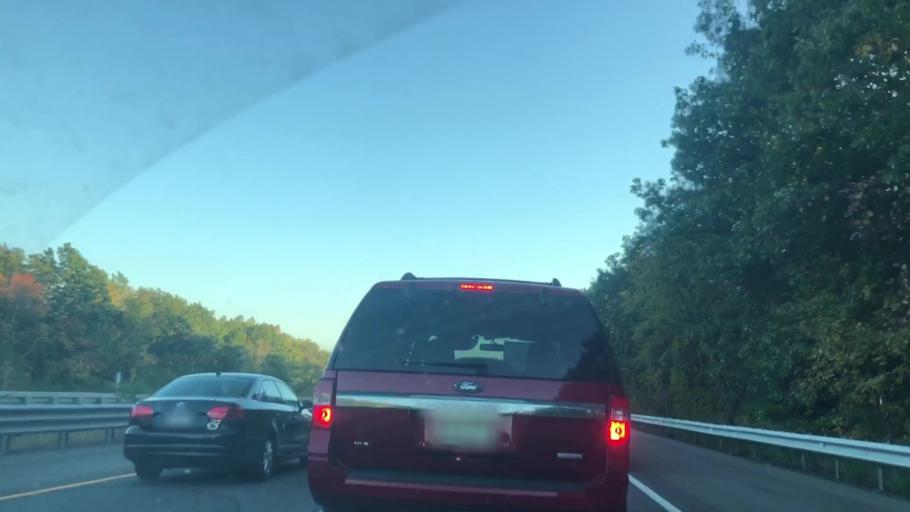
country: US
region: Massachusetts
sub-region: Franklin County
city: South Deerfield
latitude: 42.5259
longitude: -72.6270
